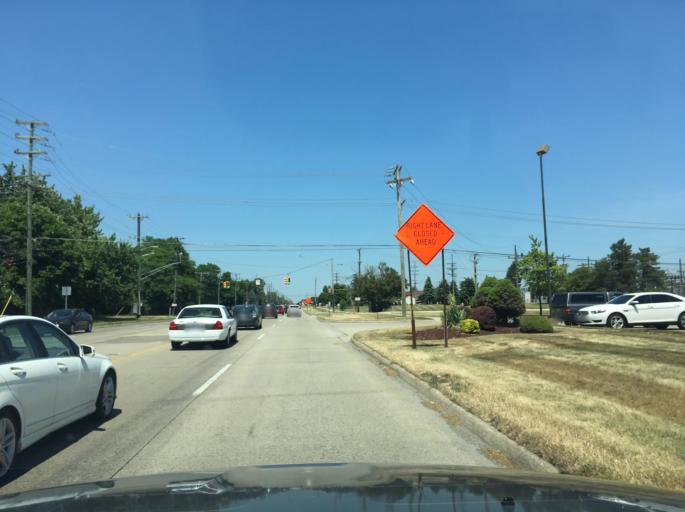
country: US
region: Michigan
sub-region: Macomb County
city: Clinton
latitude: 42.5906
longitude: -82.9520
